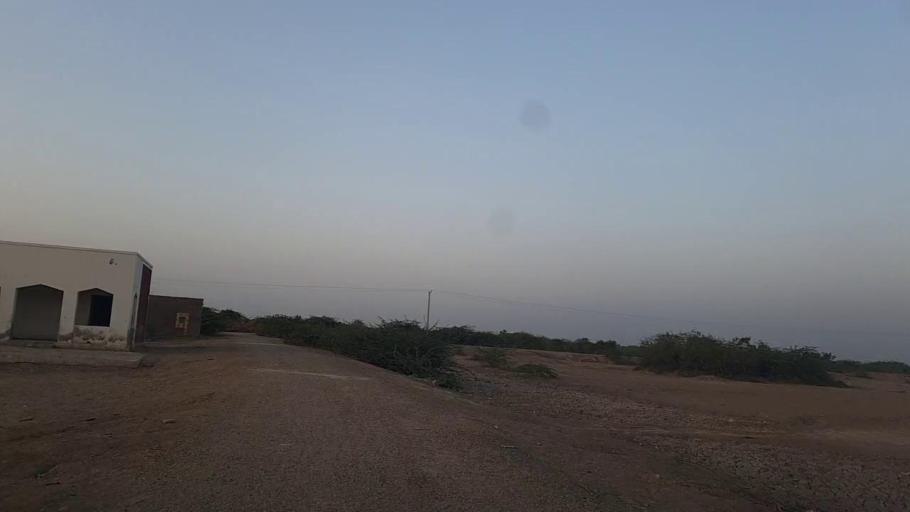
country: PK
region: Sindh
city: Naukot
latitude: 24.7189
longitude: 69.2894
